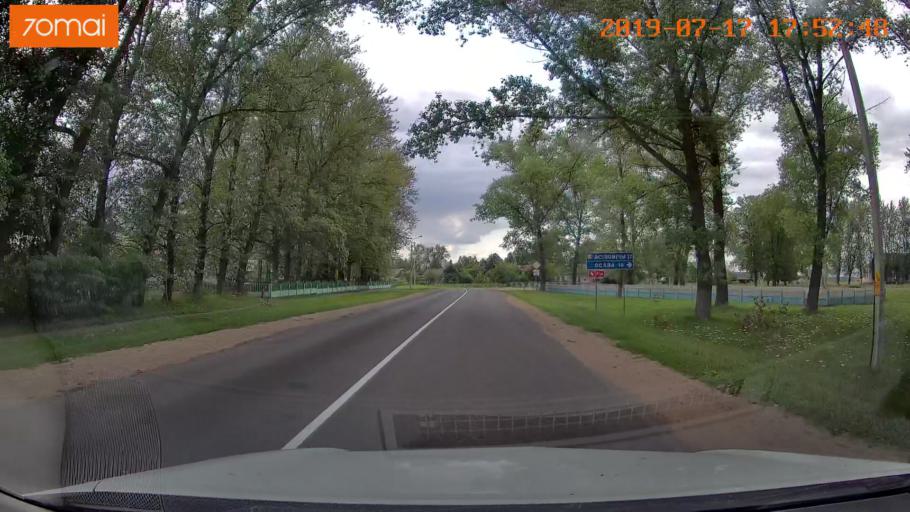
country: BY
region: Mogilev
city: Hlusha
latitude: 53.1684
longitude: 28.7791
